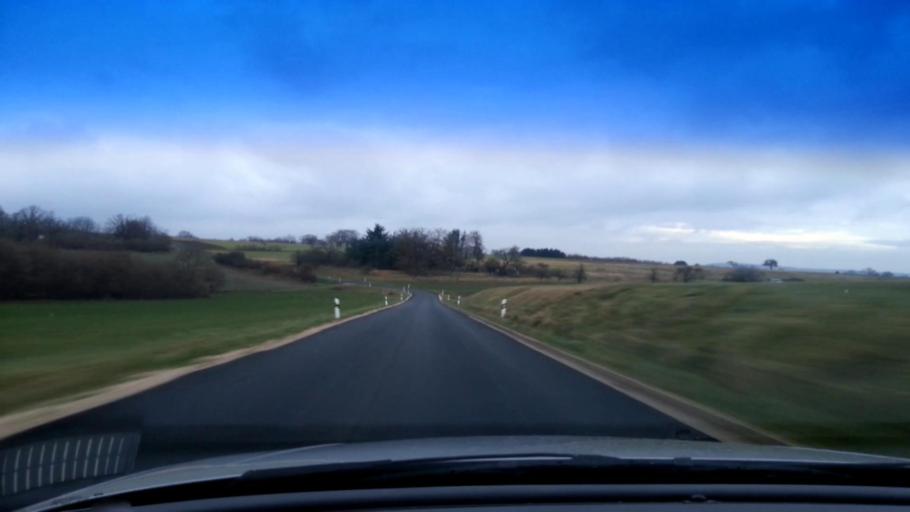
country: DE
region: Bavaria
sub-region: Upper Franconia
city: Viereth-Trunstadt
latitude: 49.9086
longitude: 10.7762
